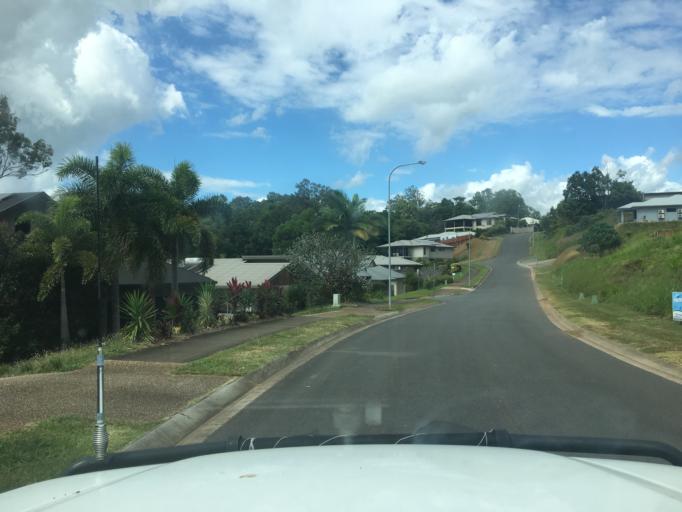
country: AU
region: Queensland
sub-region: Cairns
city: Woree
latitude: -16.9704
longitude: 145.7401
